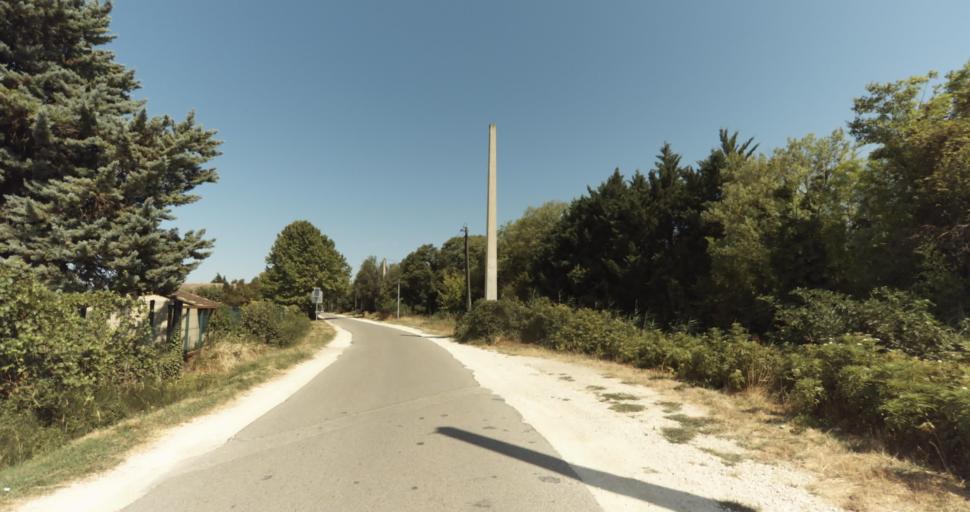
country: FR
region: Provence-Alpes-Cote d'Azur
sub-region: Departement du Vaucluse
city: Monteux
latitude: 44.0225
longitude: 4.9754
